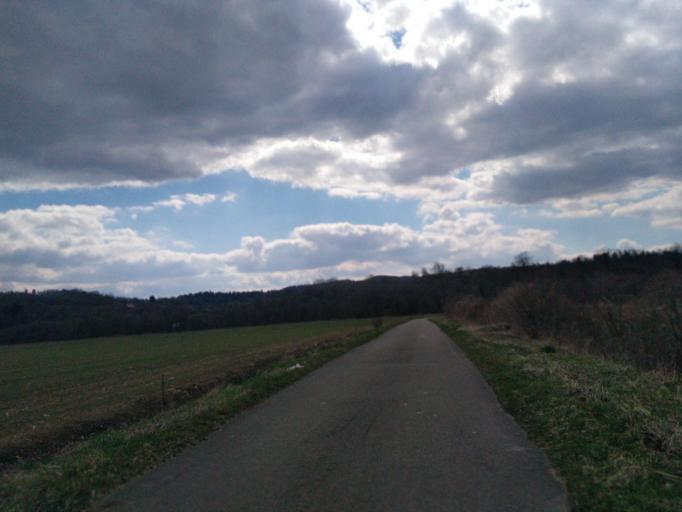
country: PL
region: Subcarpathian Voivodeship
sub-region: Powiat brzozowski
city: Dydnia
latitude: 49.6698
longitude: 22.2622
